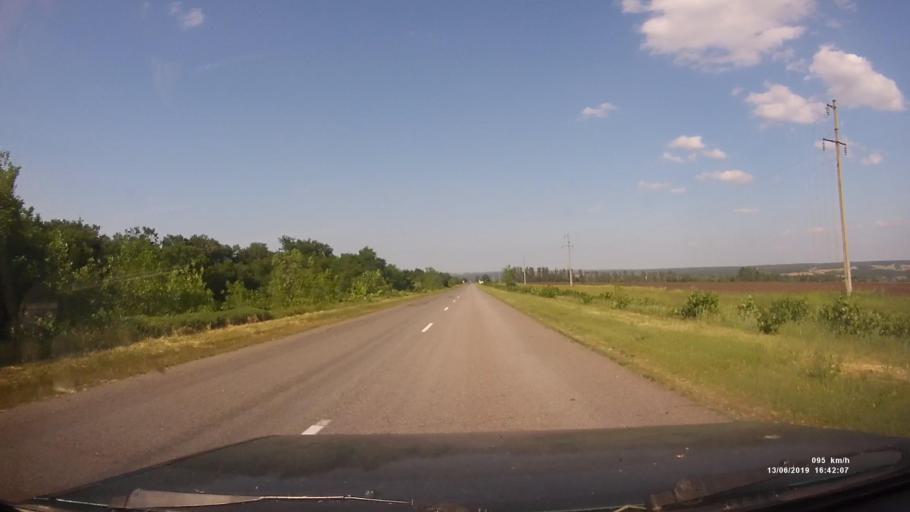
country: RU
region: Rostov
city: Kazanskaya
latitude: 49.9401
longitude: 41.3975
